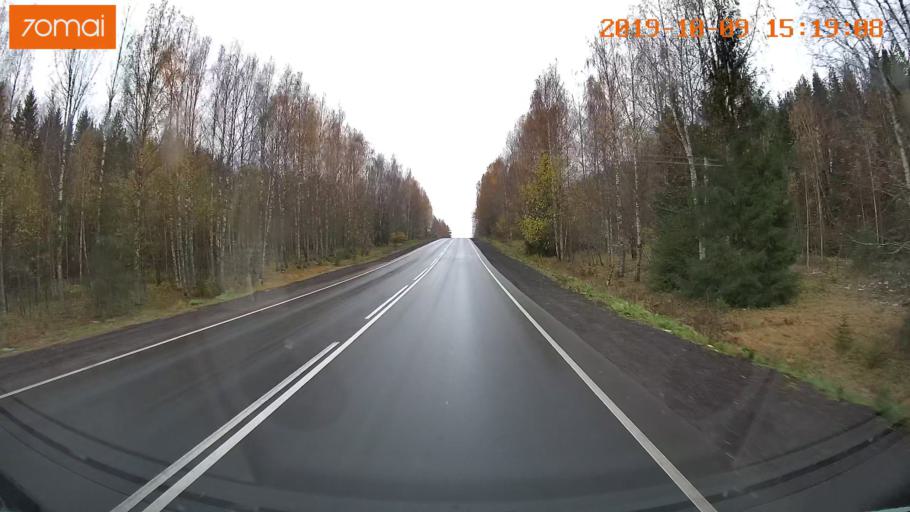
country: RU
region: Kostroma
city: Susanino
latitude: 58.0789
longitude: 41.5617
